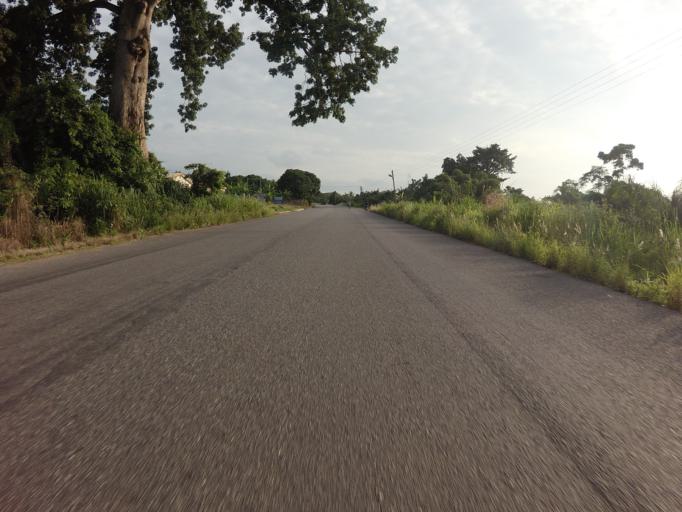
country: GH
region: Volta
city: Kpandu
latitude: 6.8909
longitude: 0.4261
